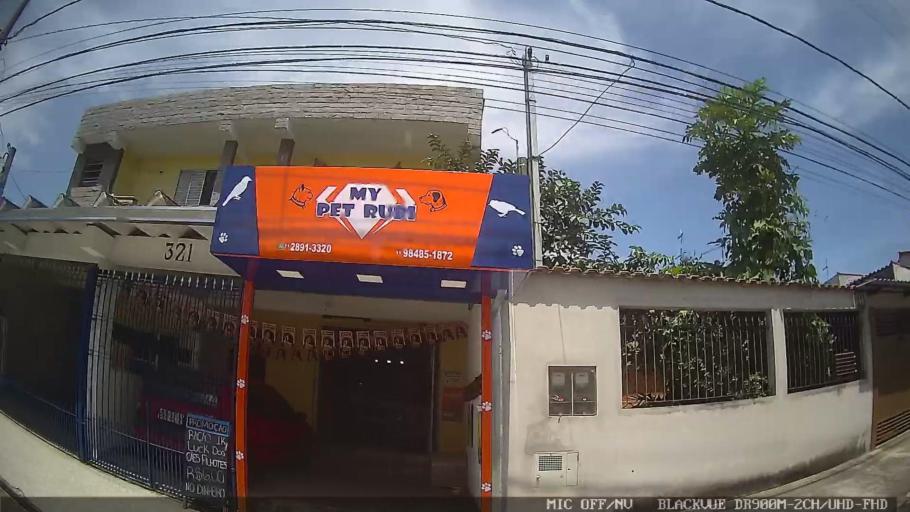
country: BR
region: Sao Paulo
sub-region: Suzano
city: Suzano
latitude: -23.5215
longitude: -46.3045
